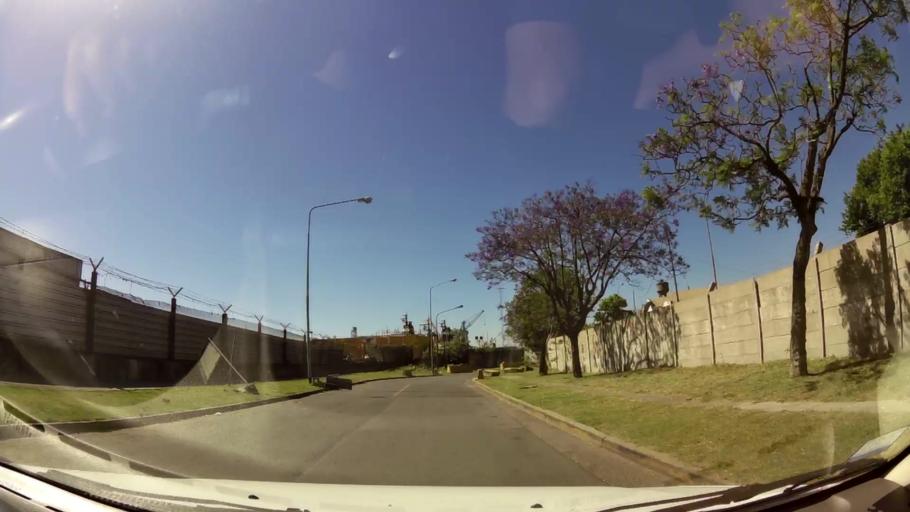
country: AR
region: Buenos Aires F.D.
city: Buenos Aires
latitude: -34.6284
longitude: -58.3496
